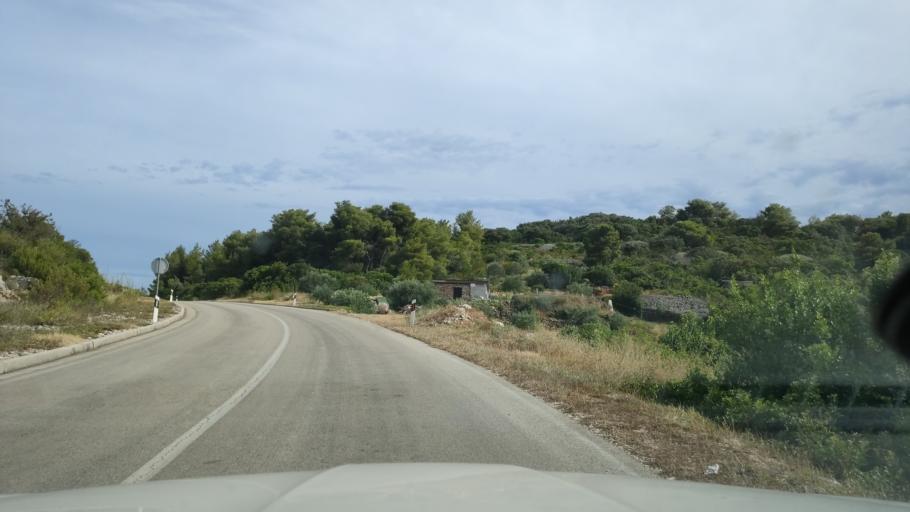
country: HR
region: Splitsko-Dalmatinska
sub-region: Grad Vis
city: Vis
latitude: 43.0379
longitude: 16.2008
